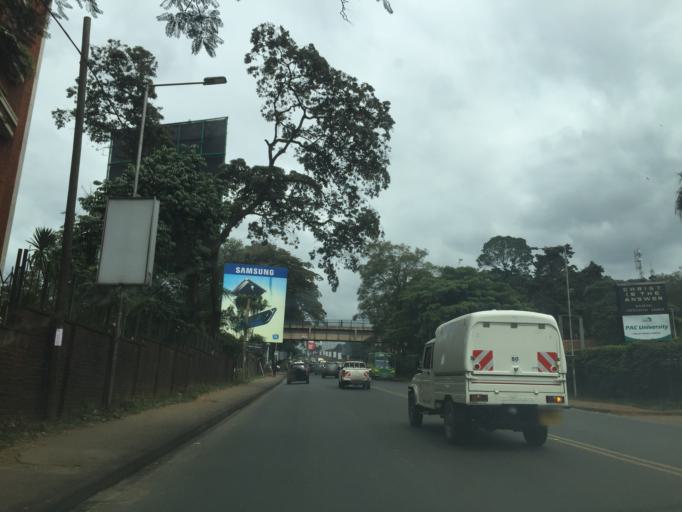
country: KE
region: Nairobi Area
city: Nairobi
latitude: -1.2919
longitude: 36.8060
